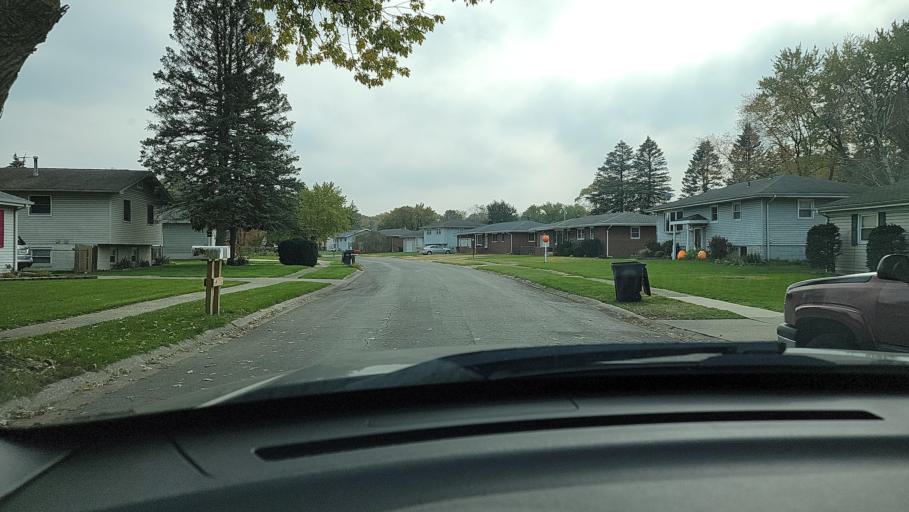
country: US
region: Indiana
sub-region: Porter County
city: Portage
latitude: 41.5907
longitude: -87.1622
